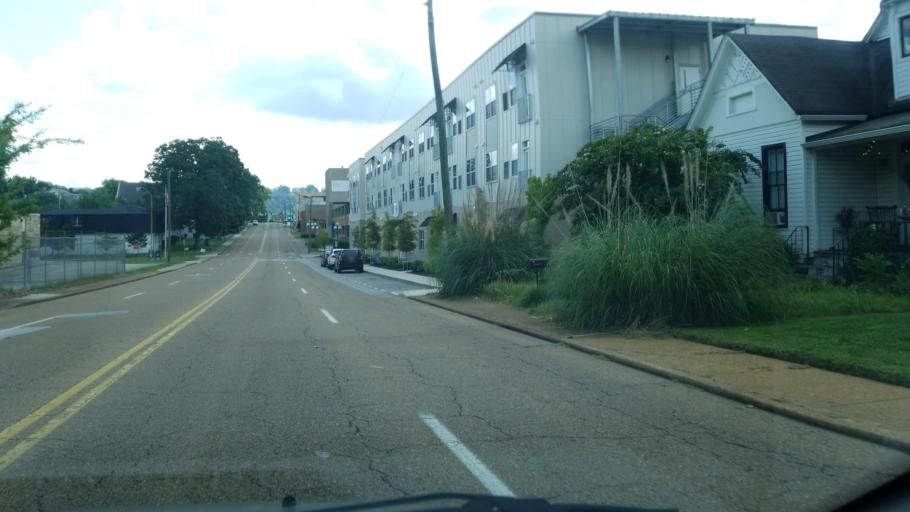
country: US
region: Tennessee
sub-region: Hamilton County
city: Chattanooga
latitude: 35.0344
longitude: -85.2788
